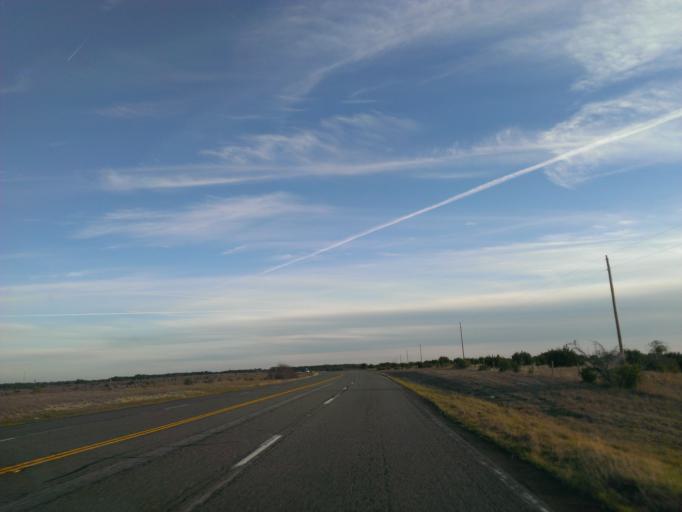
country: US
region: Texas
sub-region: Lampasas County
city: Kempner
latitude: 30.9054
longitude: -97.9711
